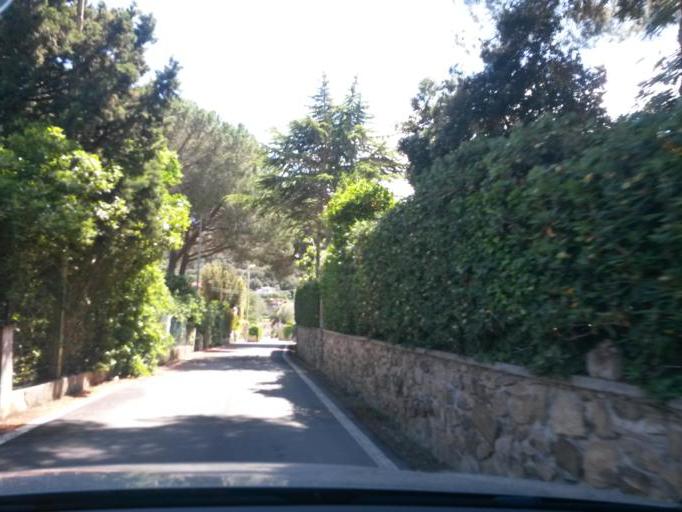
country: IT
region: Tuscany
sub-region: Provincia di Livorno
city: Rio Marina
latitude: 42.8608
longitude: 10.4186
